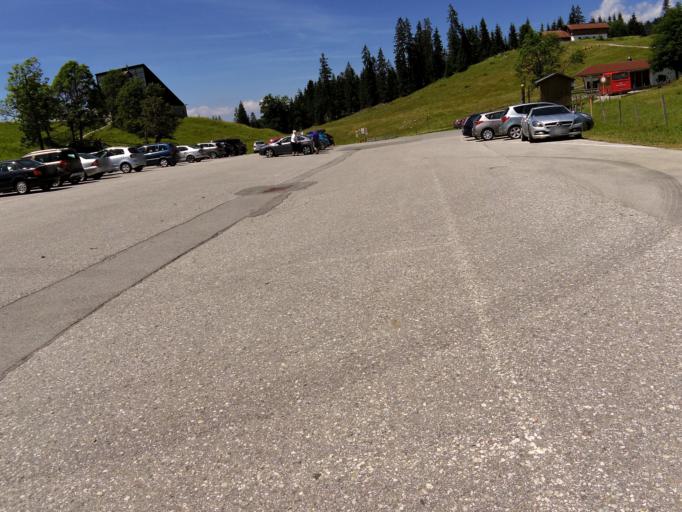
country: AT
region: Tyrol
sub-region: Politischer Bezirk Kitzbuhel
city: Waidring
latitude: 47.6574
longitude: 12.5798
